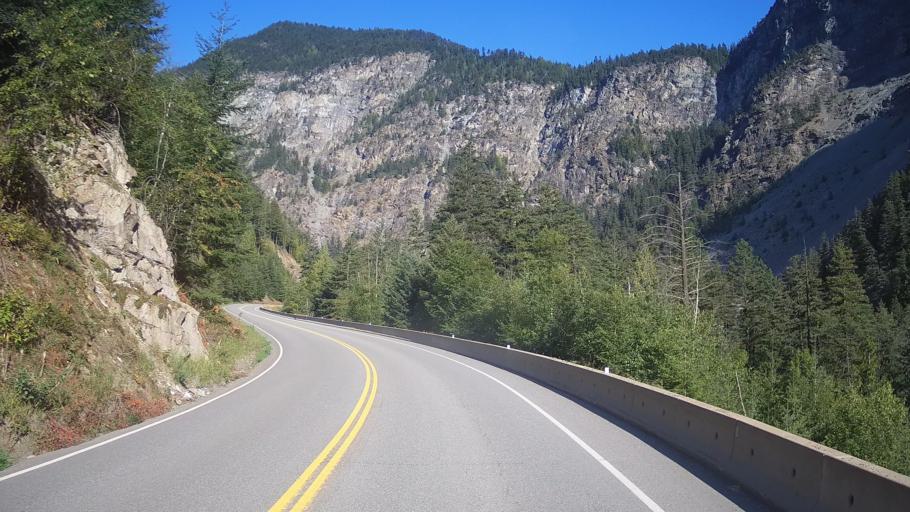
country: CA
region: British Columbia
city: Lillooet
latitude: 50.6427
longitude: -122.0551
